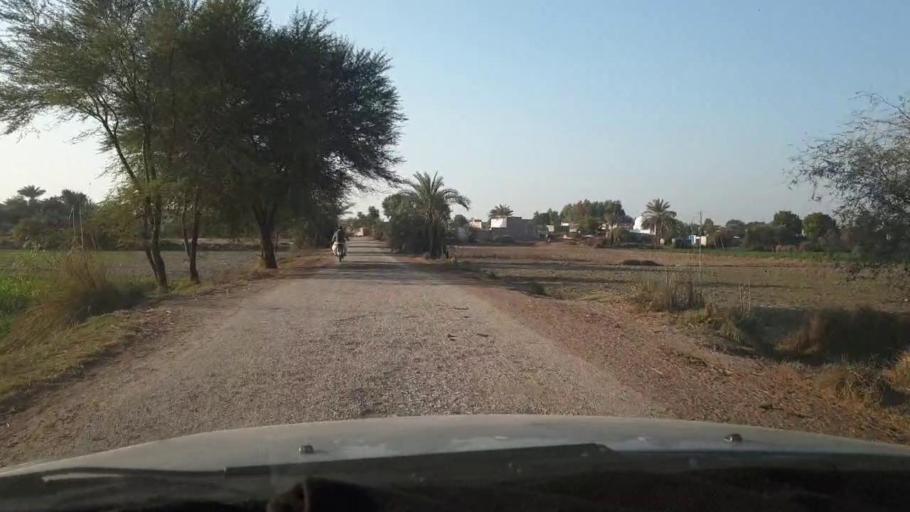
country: PK
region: Sindh
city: Mirpur Mathelo
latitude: 27.9972
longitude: 69.5170
